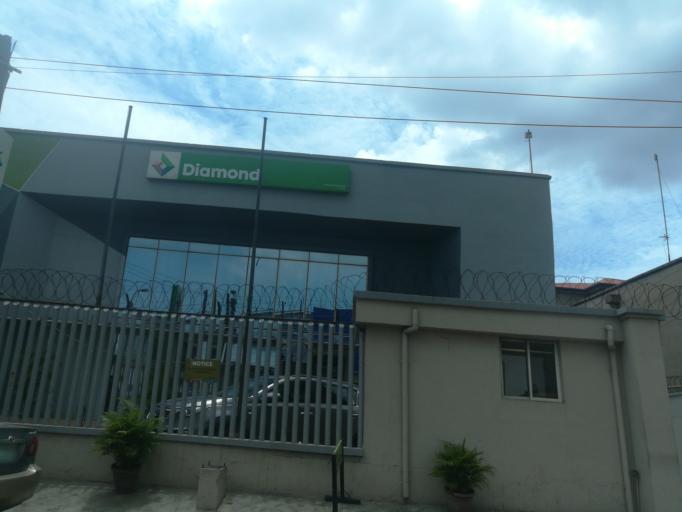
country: NG
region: Lagos
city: Ojota
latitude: 6.5886
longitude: 3.3618
